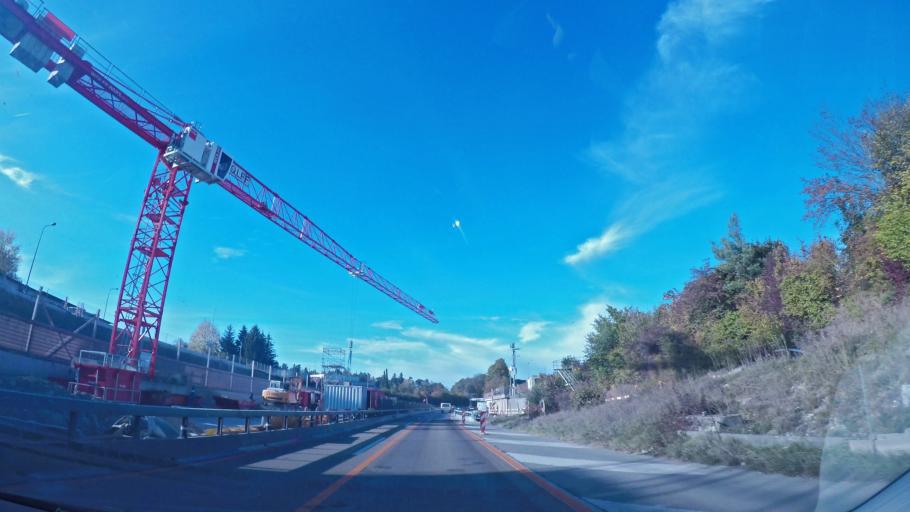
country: CH
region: Bern
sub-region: Thun District
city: Thierachern
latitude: 46.7596
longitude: 7.5960
